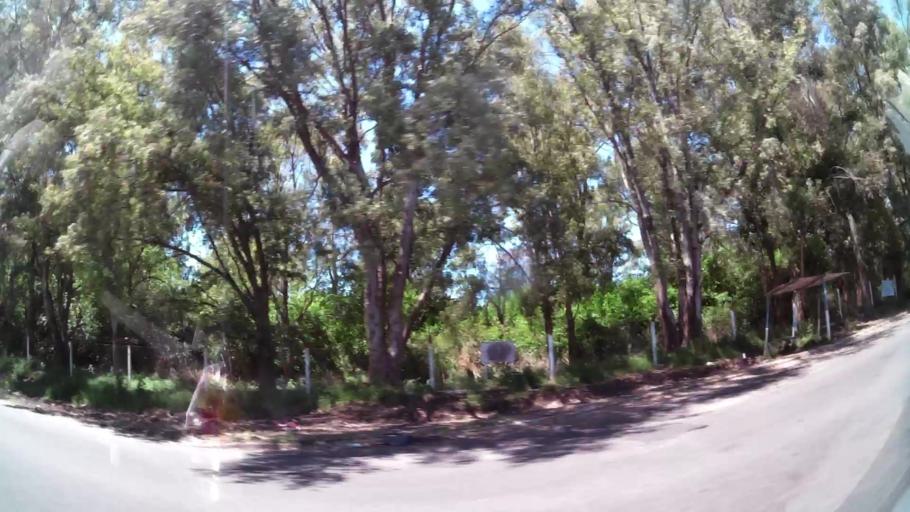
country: AR
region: Buenos Aires
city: Hurlingham
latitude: -34.5166
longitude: -58.6690
